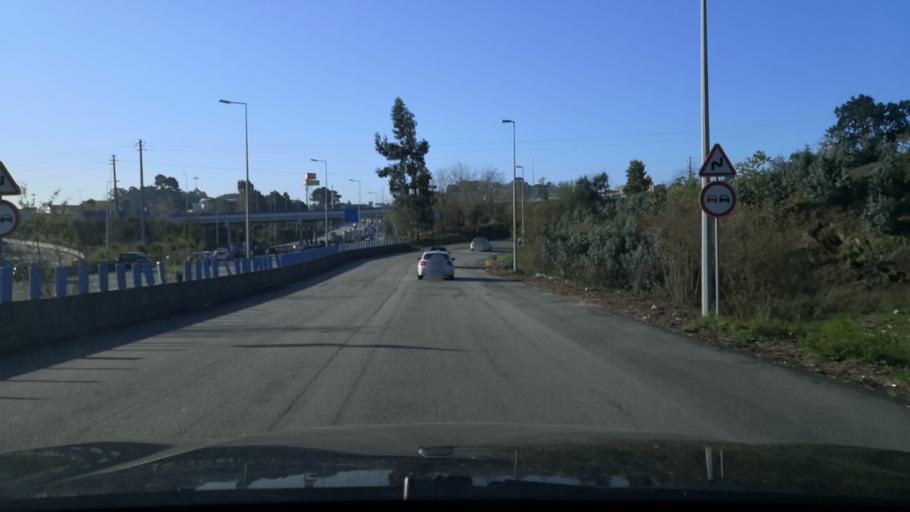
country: PT
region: Porto
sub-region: Maia
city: Leca do Bailio
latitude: 41.2047
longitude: -8.6278
